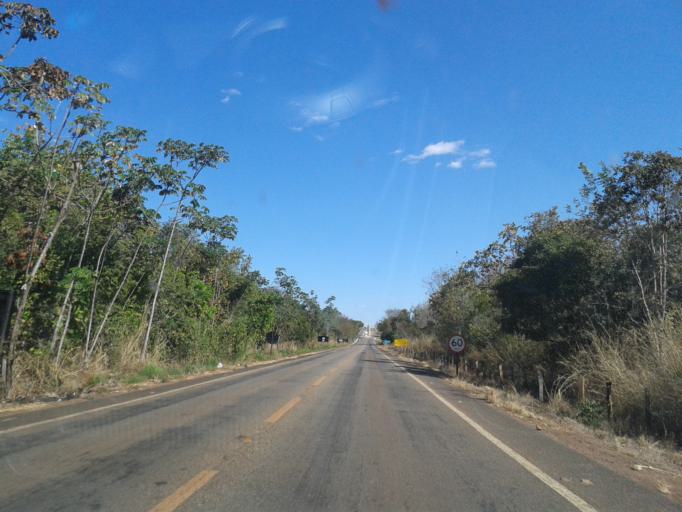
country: BR
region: Goias
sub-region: Crixas
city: Crixas
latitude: -14.0847
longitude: -50.3344
